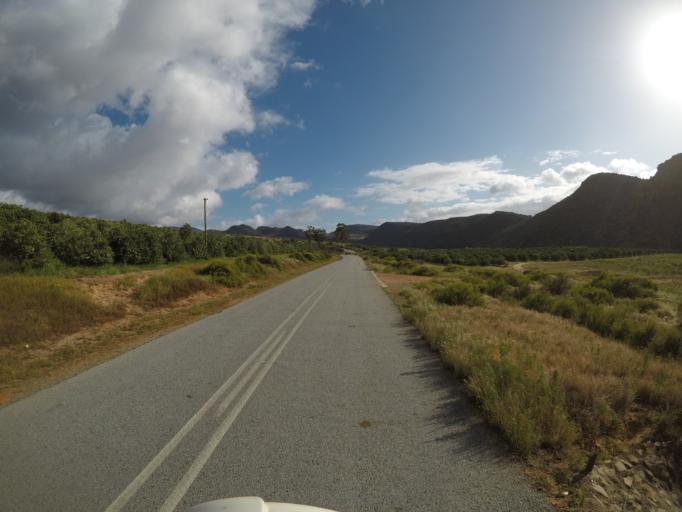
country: ZA
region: Western Cape
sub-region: West Coast District Municipality
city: Clanwilliam
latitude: -32.4353
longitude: 18.9393
